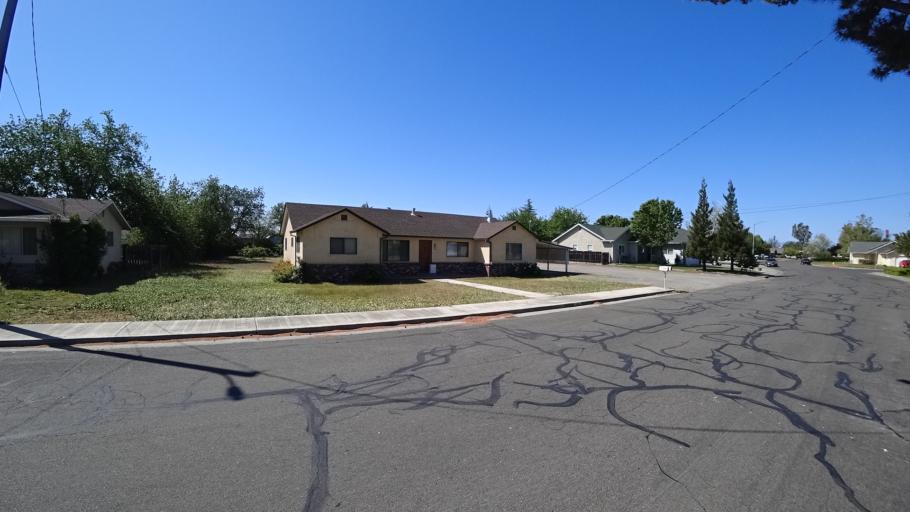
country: US
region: California
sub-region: Glenn County
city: Orland
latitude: 39.7530
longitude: -122.2005
